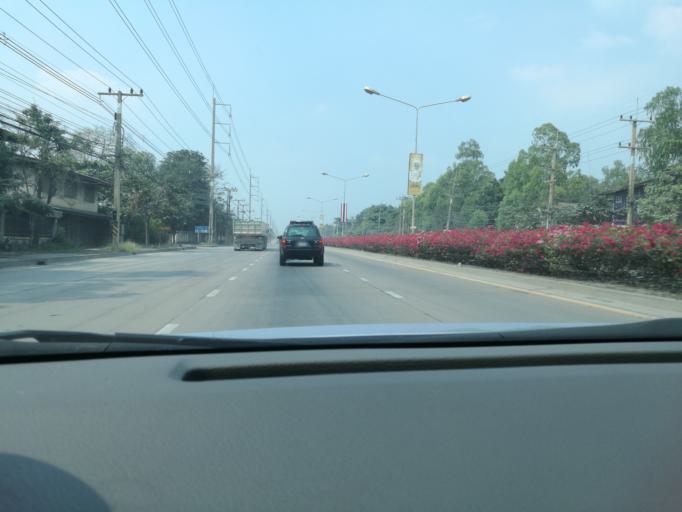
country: TH
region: Sara Buri
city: Phra Phutthabat
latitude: 14.7006
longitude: 100.8576
